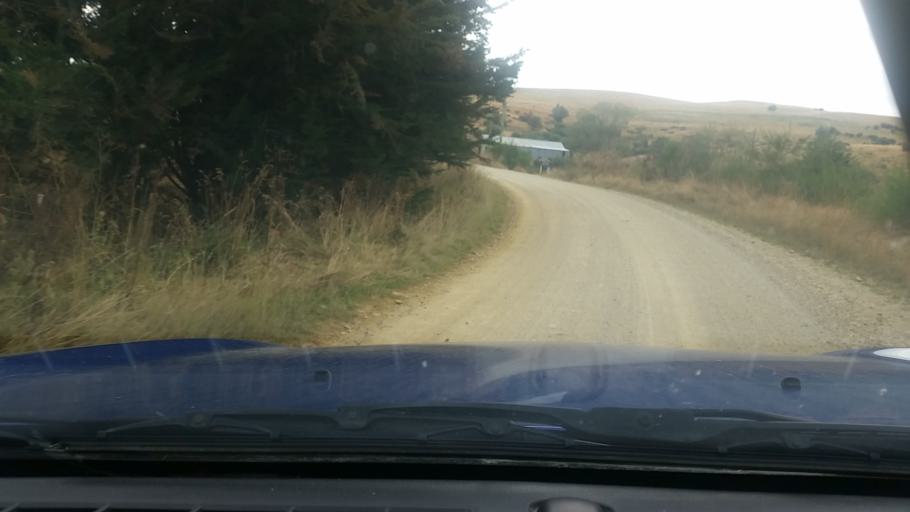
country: NZ
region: Otago
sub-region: Clutha District
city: Balclutha
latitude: -45.6952
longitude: 169.4461
